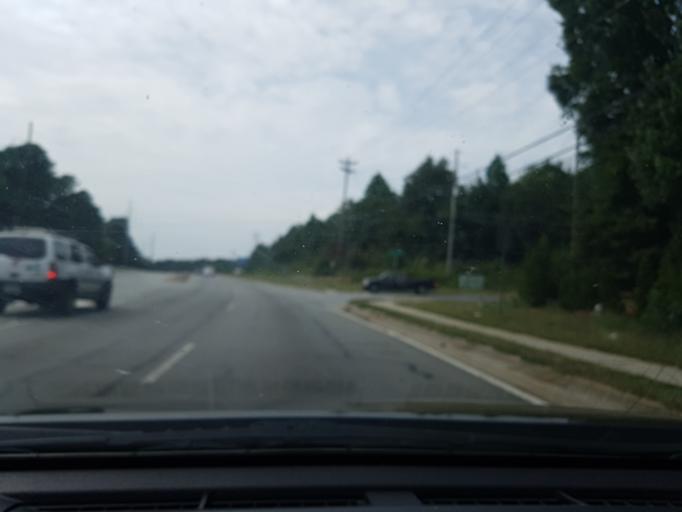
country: US
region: Georgia
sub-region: Gwinnett County
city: Lilburn
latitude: 33.9282
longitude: -84.1390
